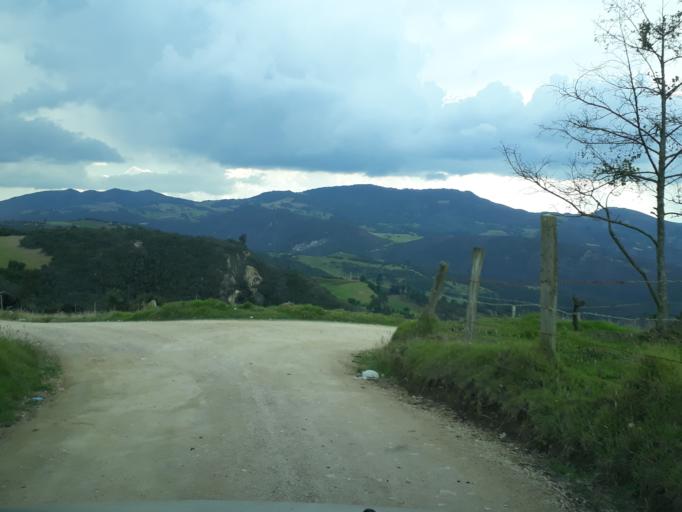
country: CO
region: Cundinamarca
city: Lenguazaque
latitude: 5.2560
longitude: -73.6904
